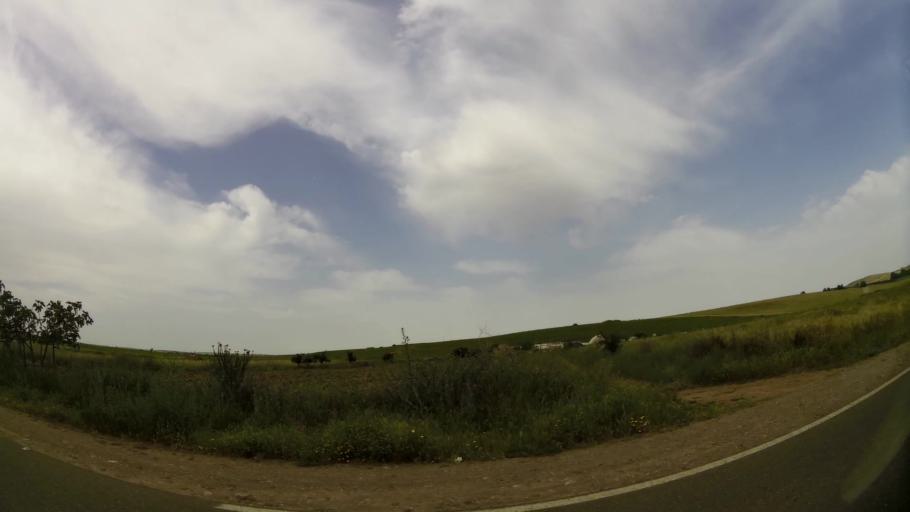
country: MA
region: Rabat-Sale-Zemmour-Zaer
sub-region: Khemisset
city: Khemisset
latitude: 33.7565
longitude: -6.2020
